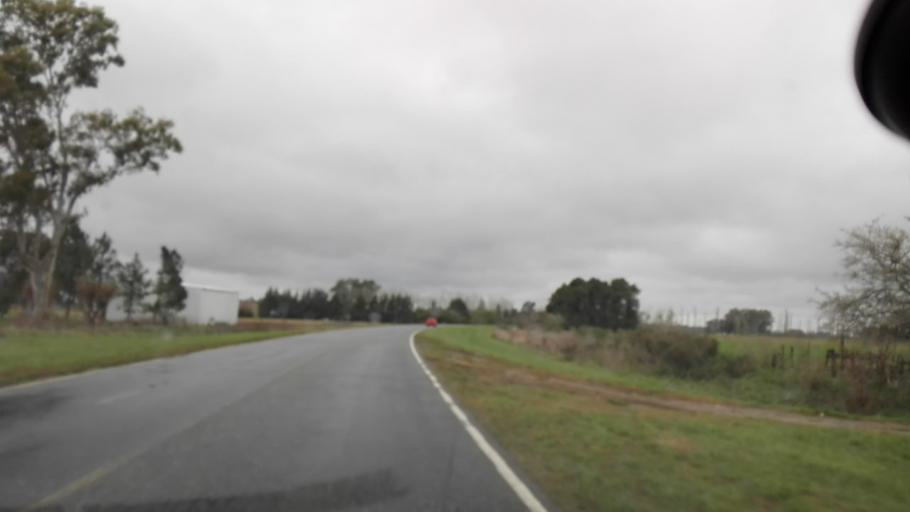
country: AR
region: Buenos Aires
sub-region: Partido de Brandsen
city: Brandsen
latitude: -35.1774
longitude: -58.2769
